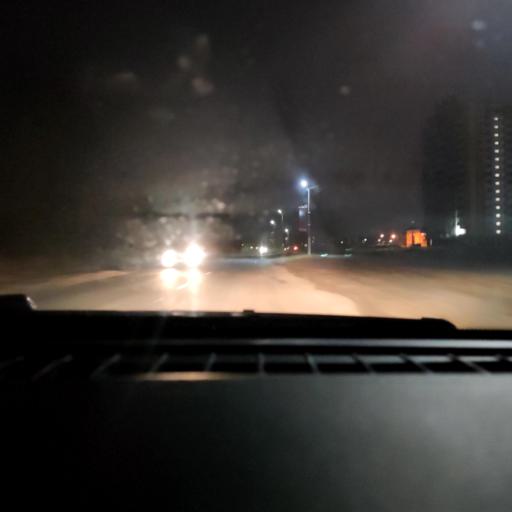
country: RU
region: Voronezj
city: Somovo
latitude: 51.6731
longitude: 39.3229
